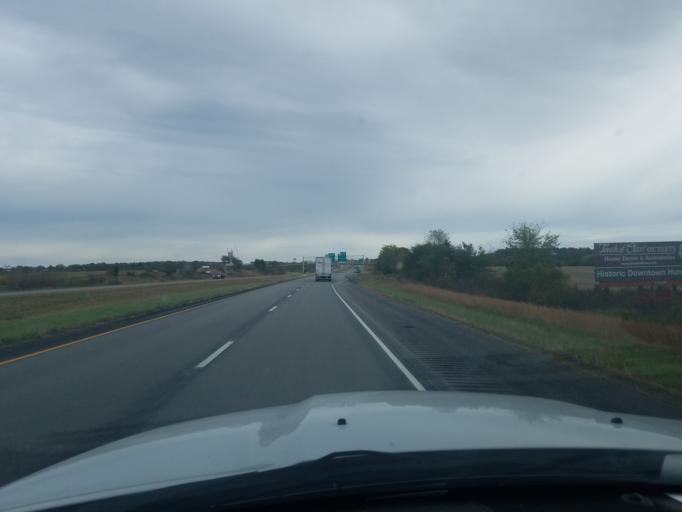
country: US
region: Indiana
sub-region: Spencer County
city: Dale
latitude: 38.1959
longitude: -86.9936
